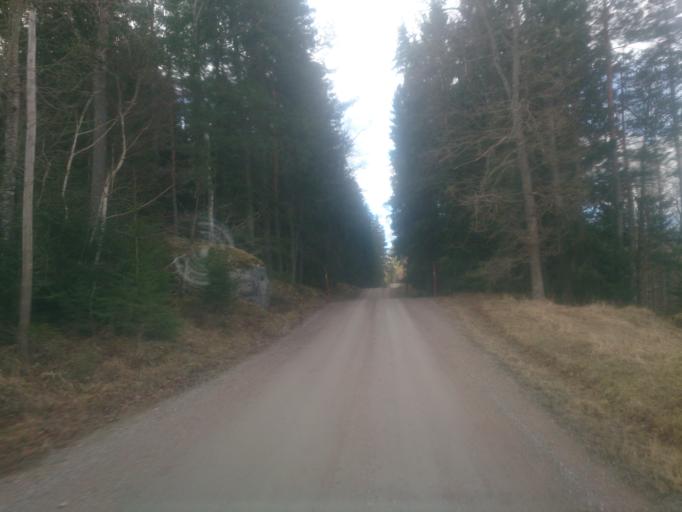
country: SE
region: OEstergoetland
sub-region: Atvidabergs Kommun
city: Atvidaberg
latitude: 58.2183
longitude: 16.1694
